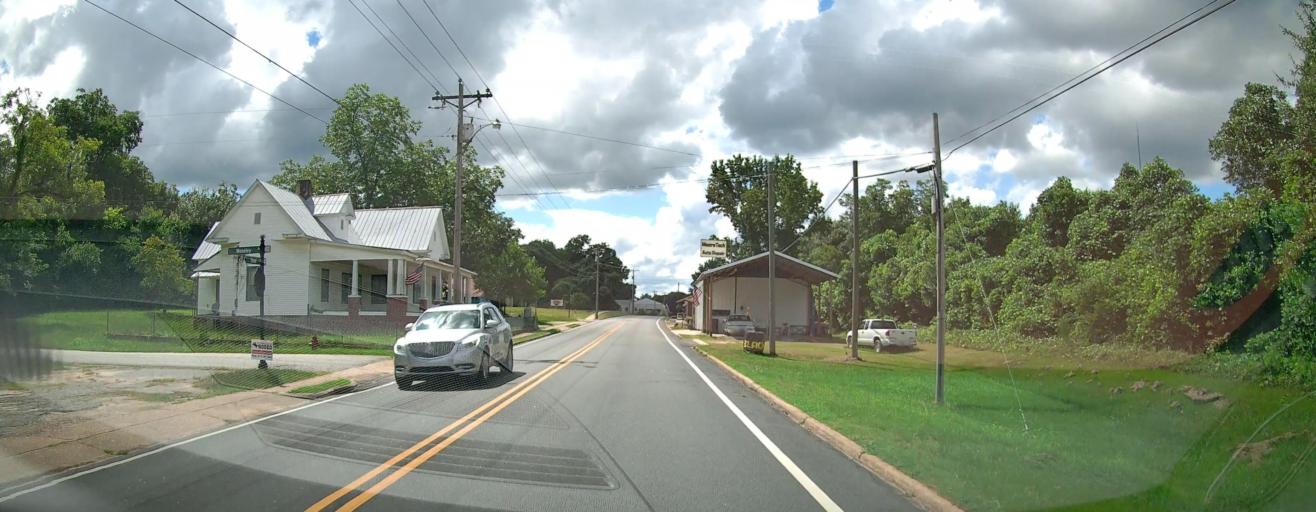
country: US
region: Georgia
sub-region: Chattahoochee County
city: Cusseta
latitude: 32.3068
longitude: -84.7796
